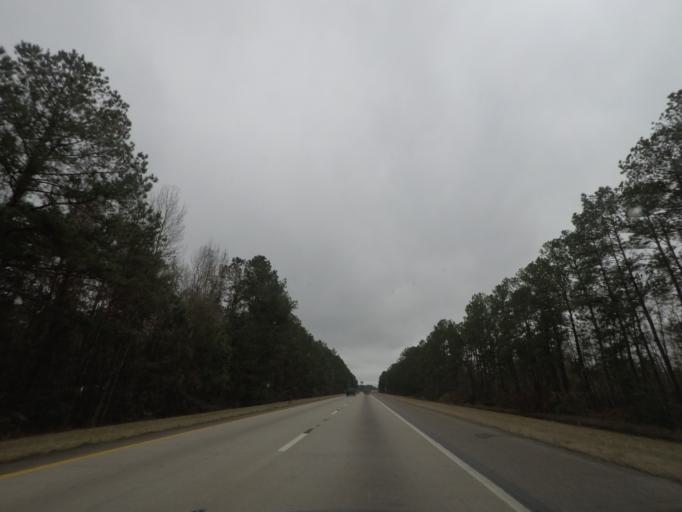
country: US
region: South Carolina
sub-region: Colleton County
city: Walterboro
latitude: 32.9684
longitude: -80.6771
